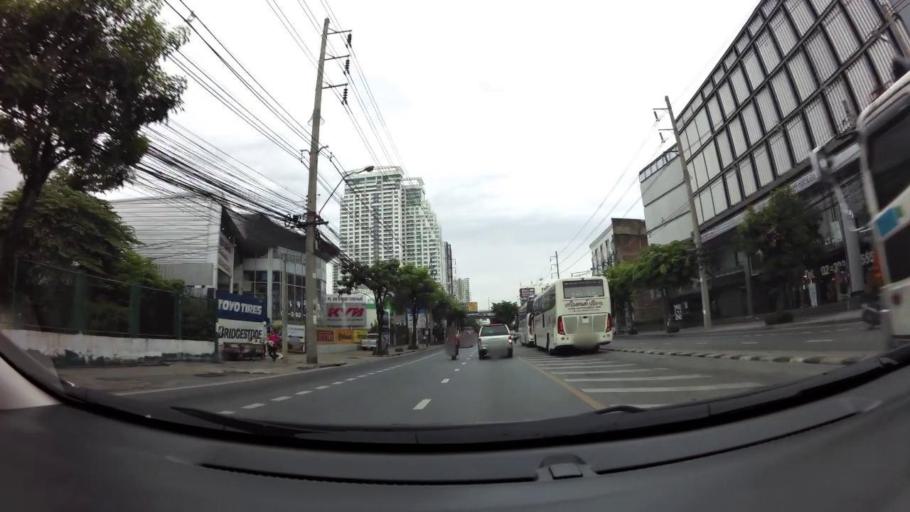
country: TH
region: Bangkok
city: Phra Khanong
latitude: 13.7127
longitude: 100.5887
